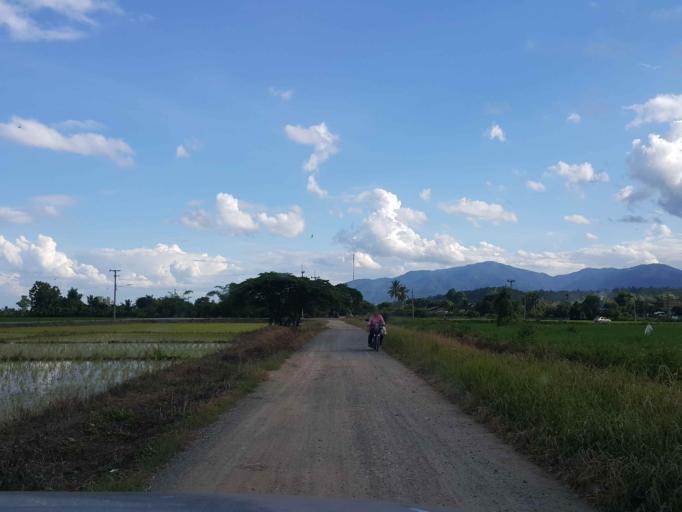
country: TH
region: Chiang Mai
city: Mae Taeng
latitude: 18.9906
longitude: 98.9491
